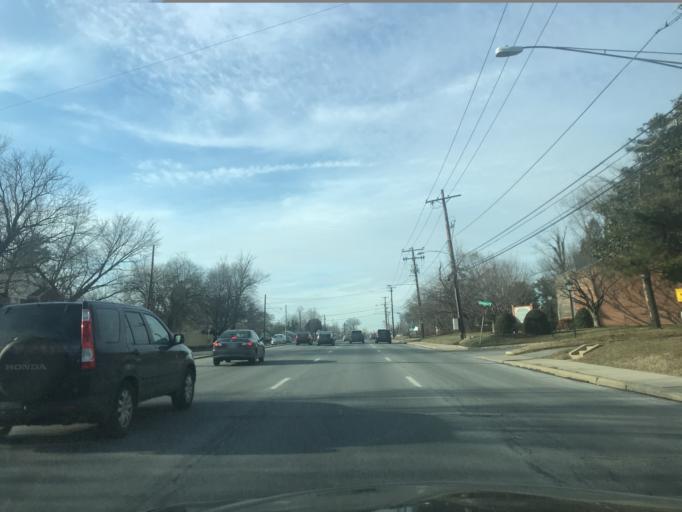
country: US
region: Maryland
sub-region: Montgomery County
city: Glenmont
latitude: 39.0656
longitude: -77.0579
